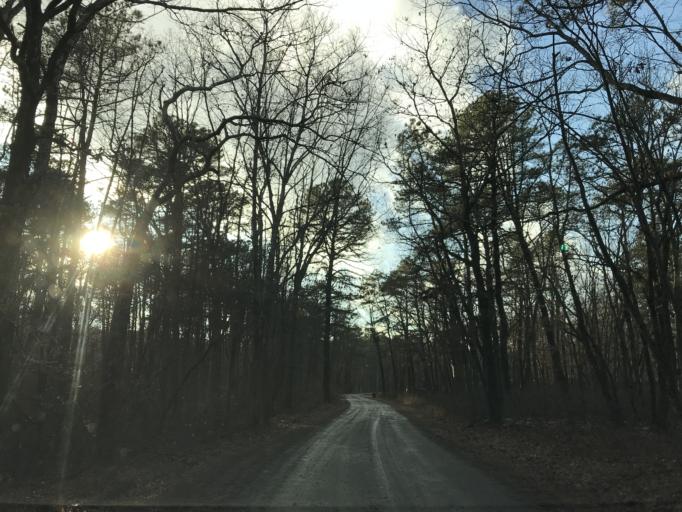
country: US
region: New Jersey
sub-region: Ocean County
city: Waretown
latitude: 39.7926
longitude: -74.2241
